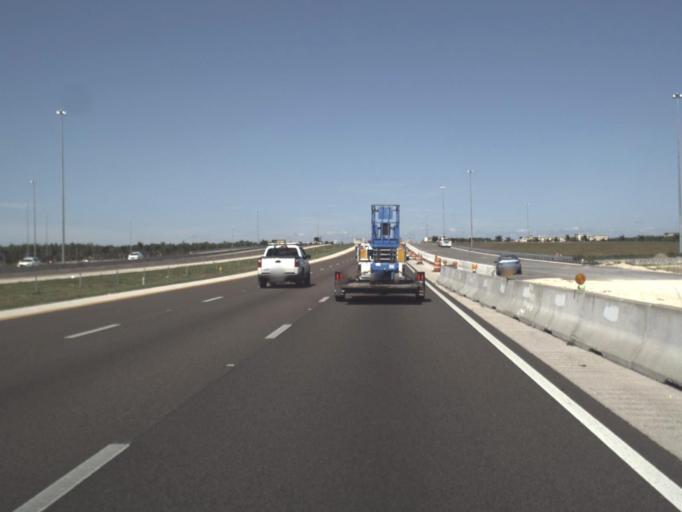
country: US
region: Florida
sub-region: Lee County
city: Three Oaks
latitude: 26.4870
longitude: -81.7942
